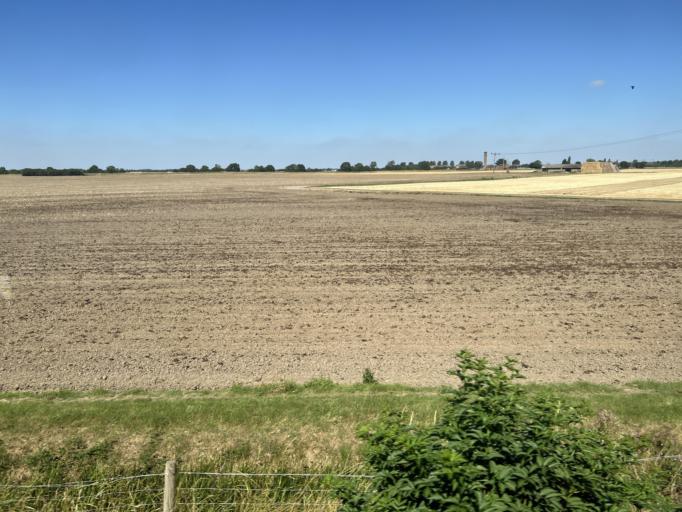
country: GB
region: England
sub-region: Lincolnshire
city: Spilsby
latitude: 53.0639
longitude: 0.0636
